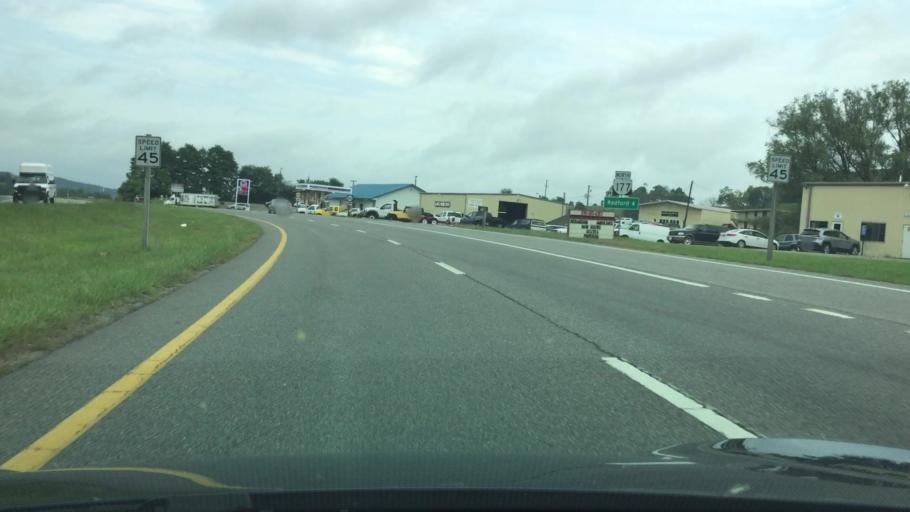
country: US
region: Virginia
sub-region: City of Radford
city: Radford
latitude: 37.0994
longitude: -80.5095
